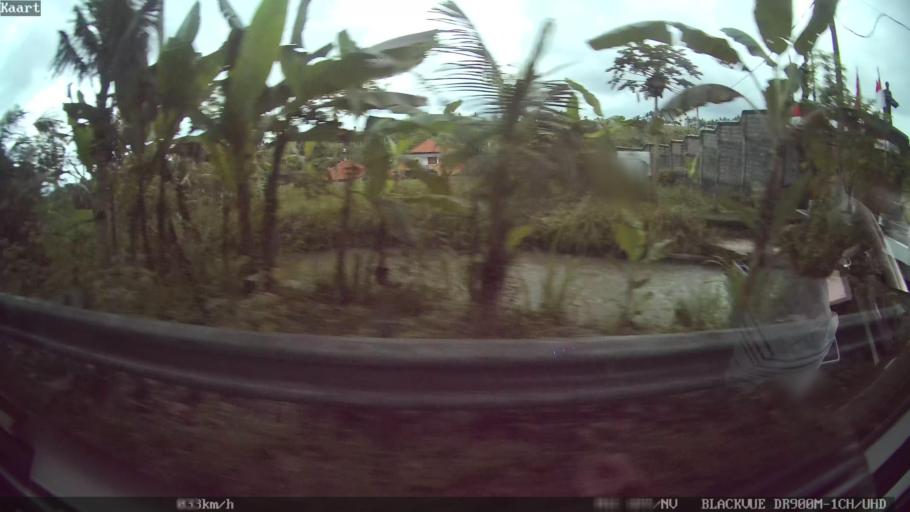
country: ID
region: Bali
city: Banjar Cemenggon
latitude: -8.5333
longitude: 115.1927
